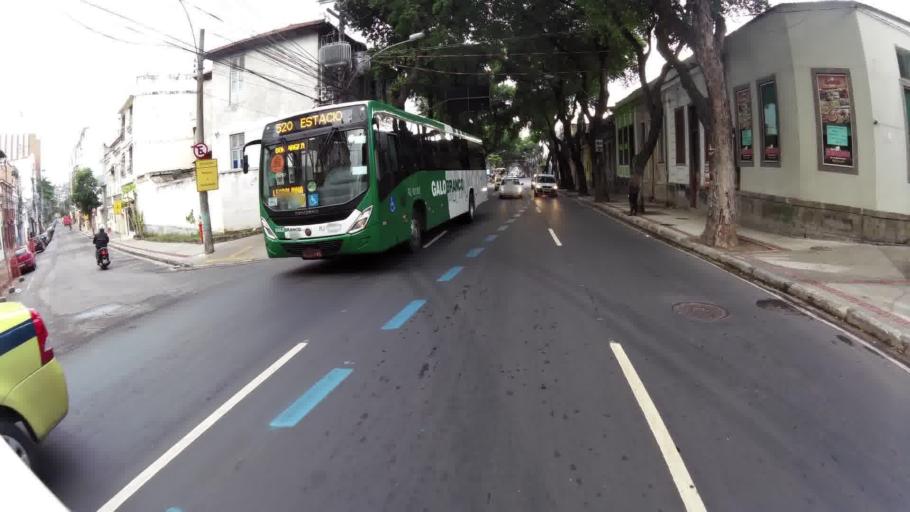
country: BR
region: Rio de Janeiro
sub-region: Rio De Janeiro
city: Rio de Janeiro
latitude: -22.9130
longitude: -43.2024
